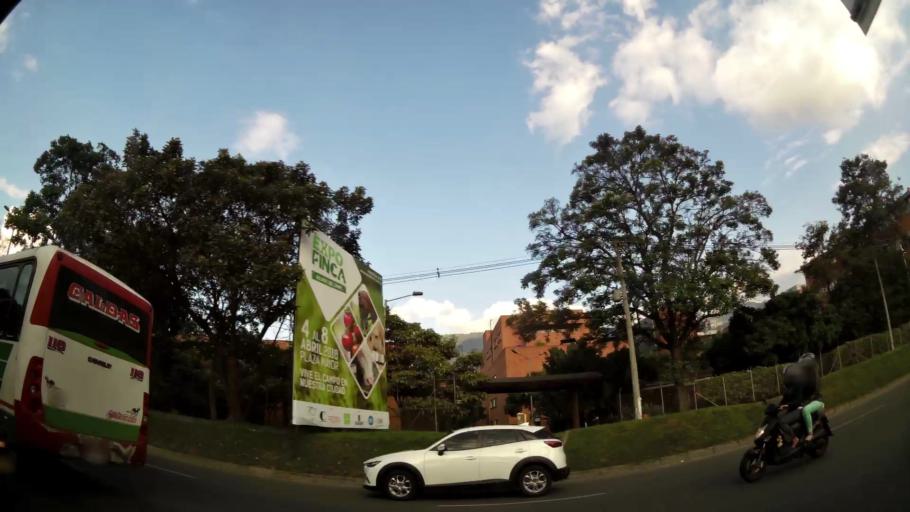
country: CO
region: Antioquia
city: Itagui
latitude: 6.2020
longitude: -75.5792
